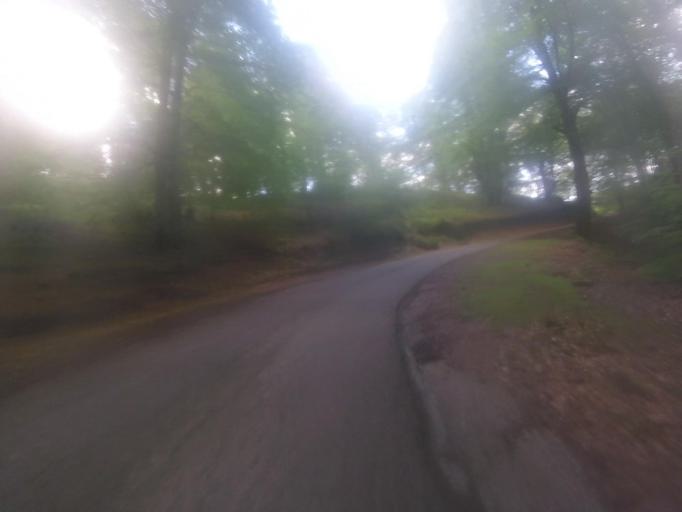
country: ES
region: Navarre
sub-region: Provincia de Navarra
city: Goizueta
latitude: 43.2277
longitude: -1.8042
